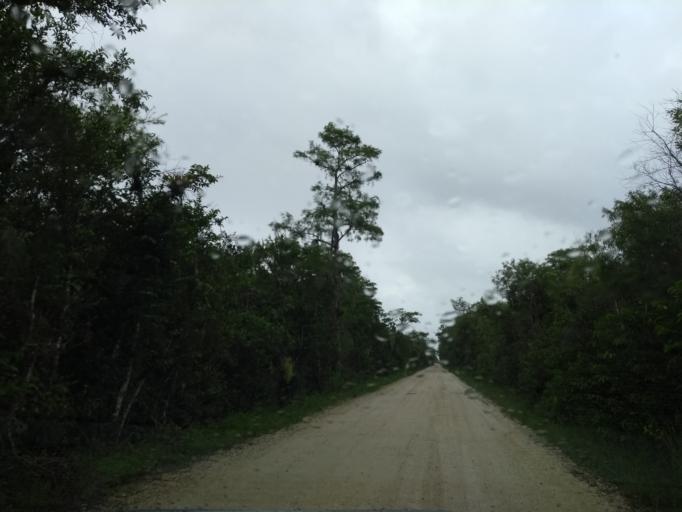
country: US
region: Florida
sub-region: Miami-Dade County
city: The Hammocks
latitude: 25.7605
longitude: -81.0052
